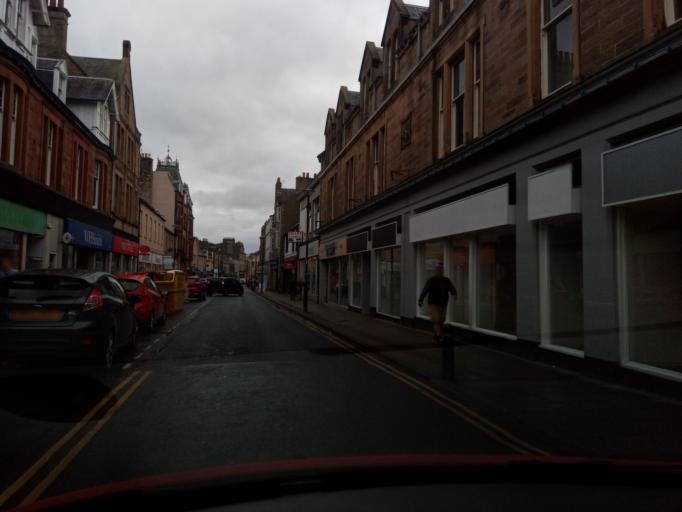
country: GB
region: Scotland
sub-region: The Scottish Borders
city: Galashiels
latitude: 55.6170
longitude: -2.8084
